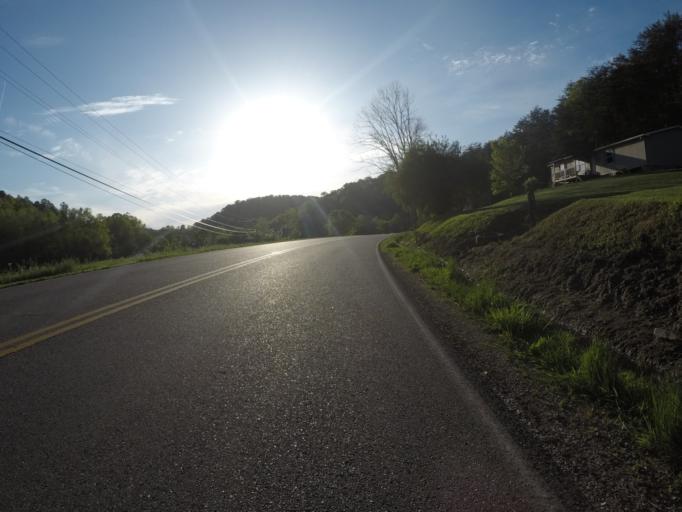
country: US
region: West Virginia
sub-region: Cabell County
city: Huntington
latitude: 38.5550
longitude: -82.4504
